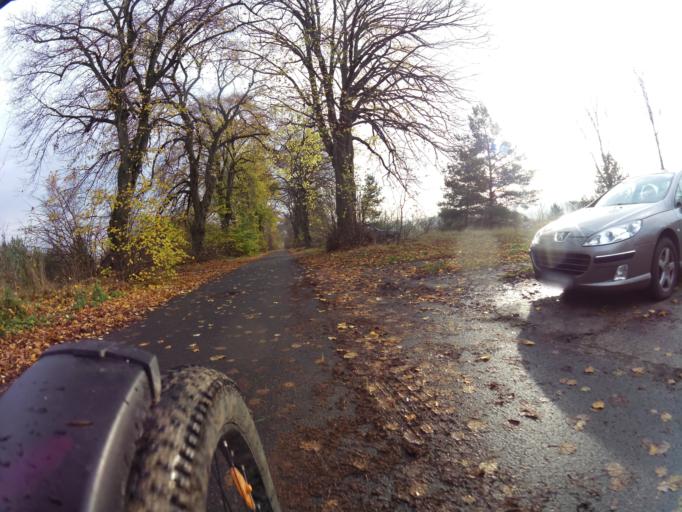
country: PL
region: Pomeranian Voivodeship
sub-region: Powiat wejherowski
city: Gniewino
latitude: 54.7132
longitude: 18.0949
